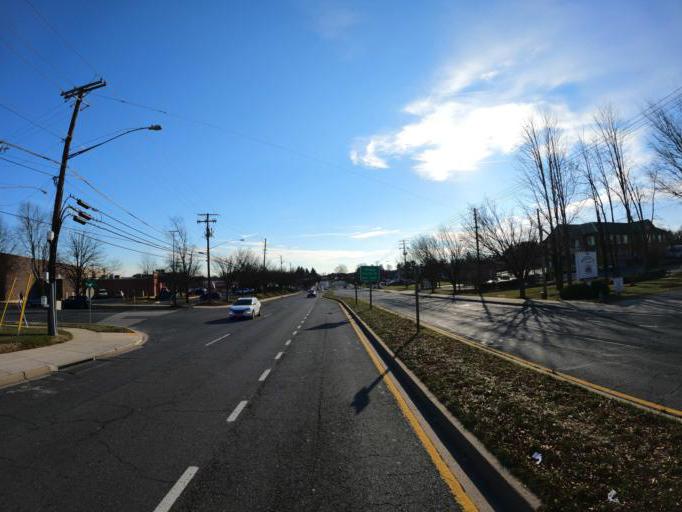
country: US
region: Maryland
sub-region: Montgomery County
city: Olney
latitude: 39.1527
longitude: -77.0658
